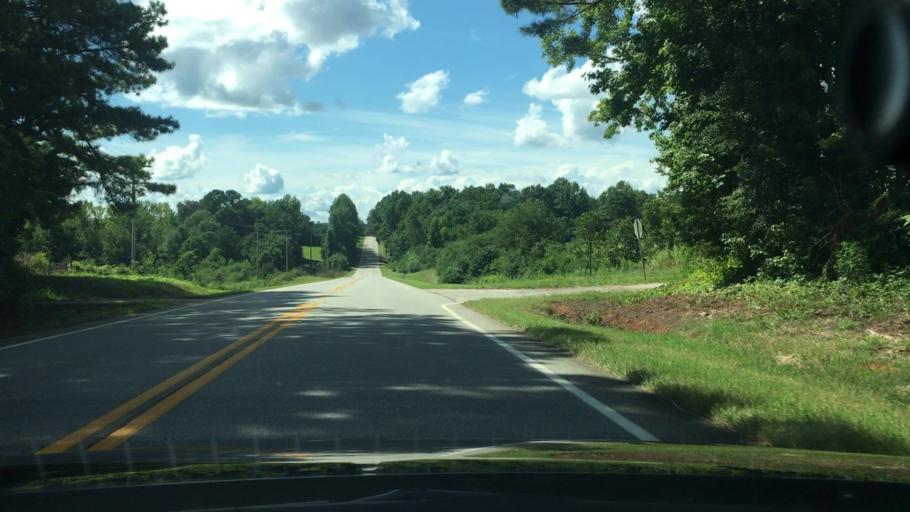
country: US
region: Georgia
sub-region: Jasper County
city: Monticello
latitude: 33.3082
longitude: -83.7396
